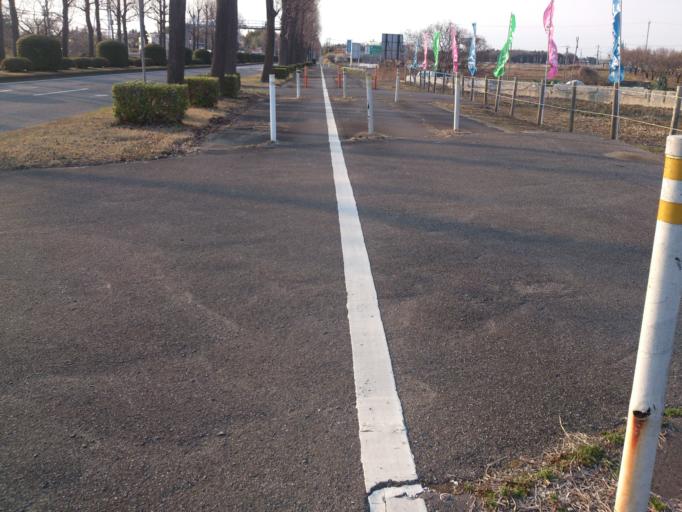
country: JP
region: Ibaraki
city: Naka
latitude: 36.0962
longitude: 140.0957
